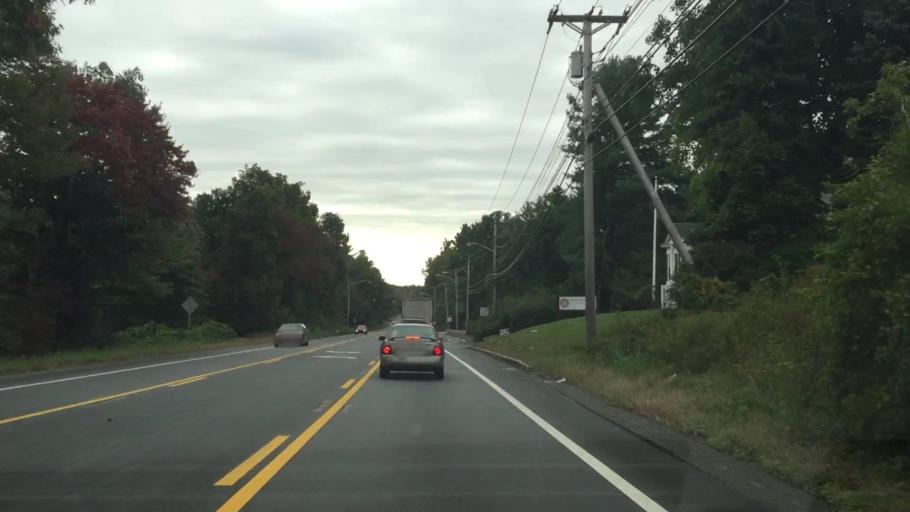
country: US
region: Massachusetts
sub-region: Essex County
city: Andover
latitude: 42.6545
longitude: -71.1002
